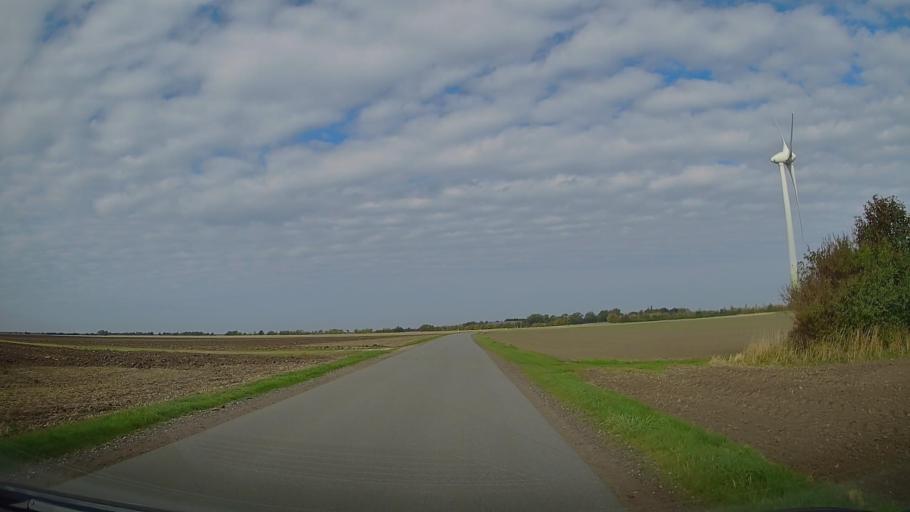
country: DE
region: Schleswig-Holstein
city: Grossenbrode
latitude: 54.5126
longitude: 11.0544
